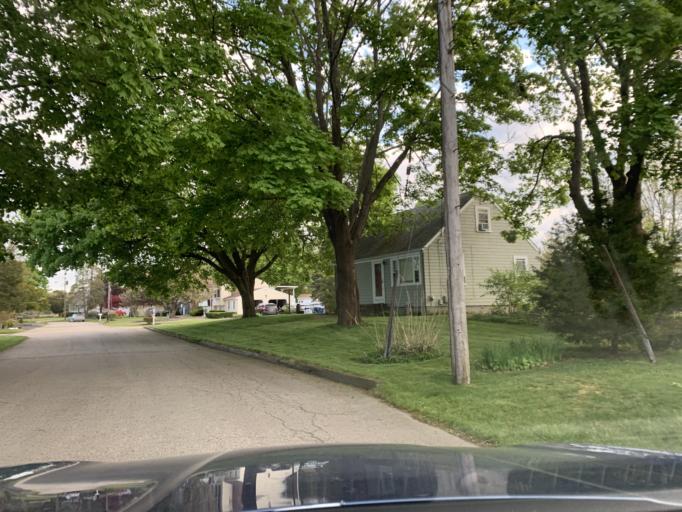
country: US
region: Rhode Island
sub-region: Kent County
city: East Greenwich
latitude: 41.6601
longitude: -71.4186
